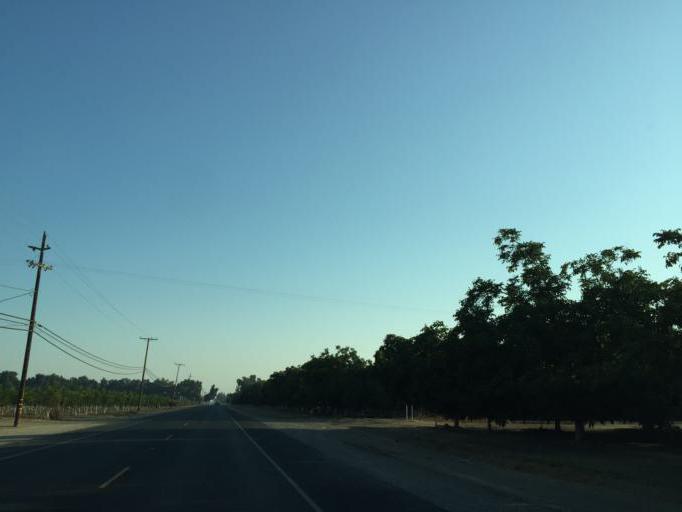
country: US
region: California
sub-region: Tulare County
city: Visalia
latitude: 36.3886
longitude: -119.2966
